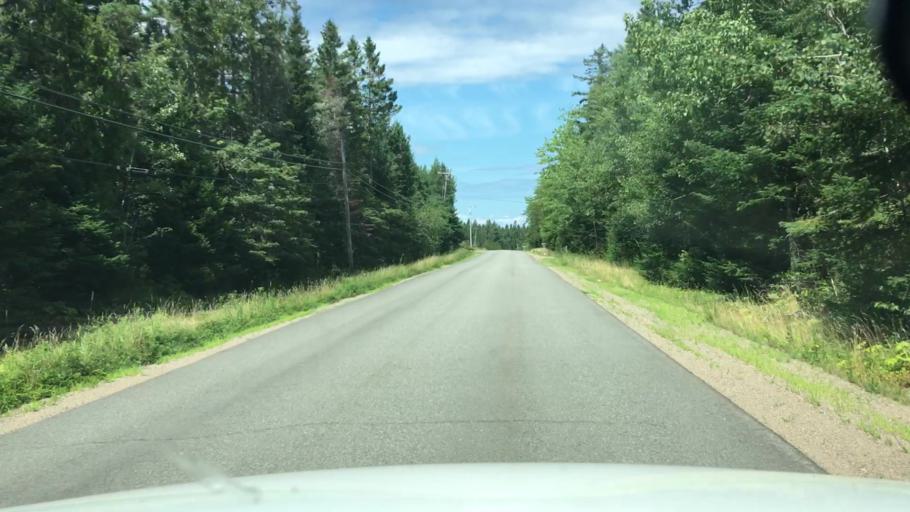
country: CA
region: New Brunswick
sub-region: Charlotte County
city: Saint Andrews
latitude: 44.9842
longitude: -67.0688
